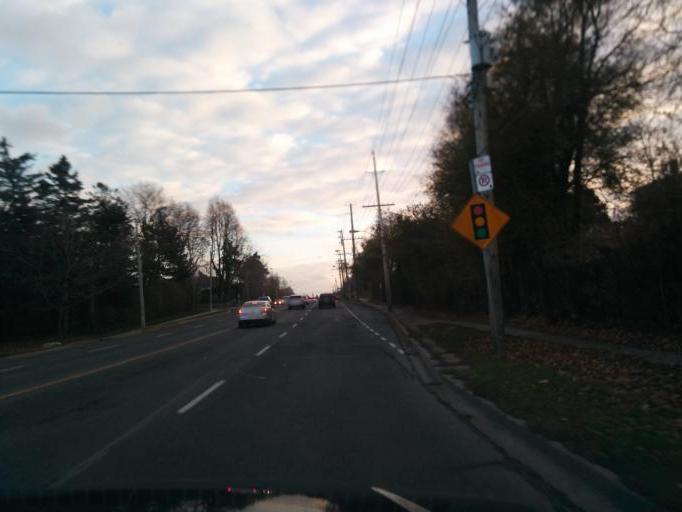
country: CA
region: Ontario
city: Etobicoke
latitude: 43.6824
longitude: -79.5402
